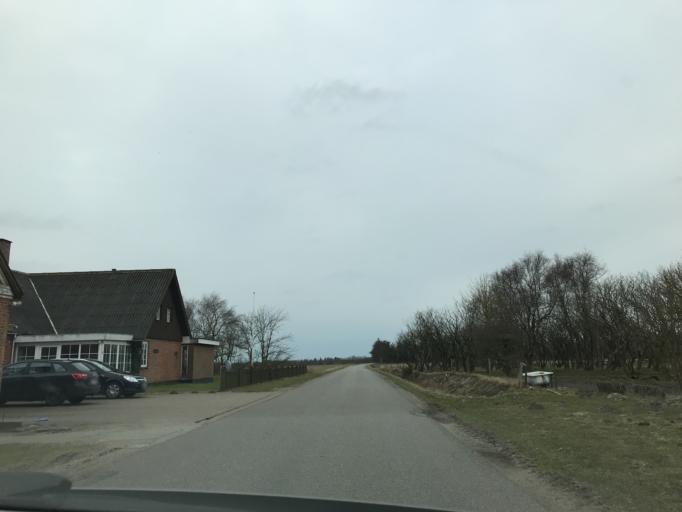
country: DK
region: South Denmark
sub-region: Varde Kommune
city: Oksbol
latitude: 55.8059
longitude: 8.3164
